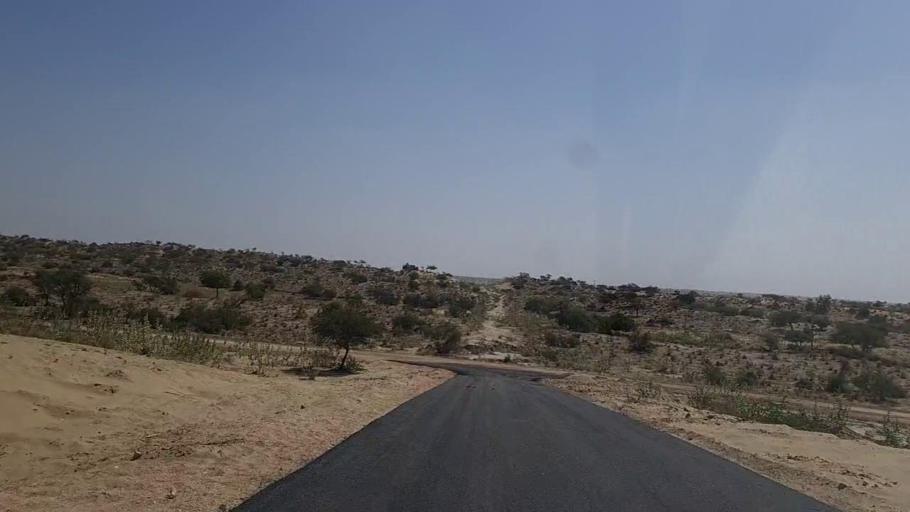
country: PK
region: Sindh
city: Diplo
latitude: 24.4782
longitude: 69.5302
